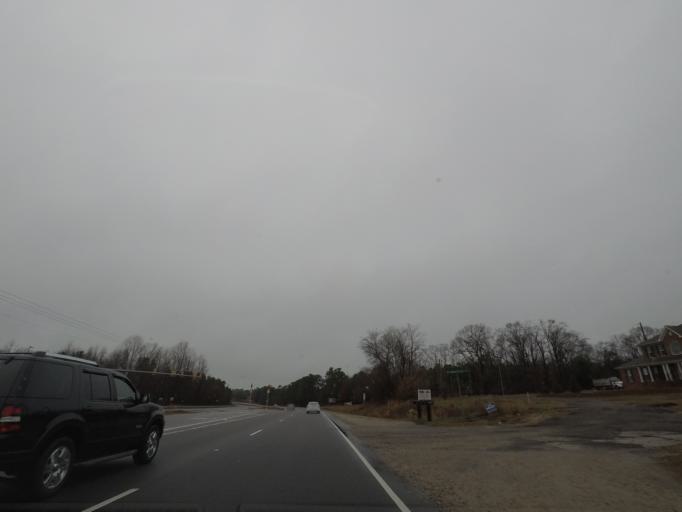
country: US
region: North Carolina
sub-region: Cumberland County
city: Spring Lake
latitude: 35.2458
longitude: -79.0228
